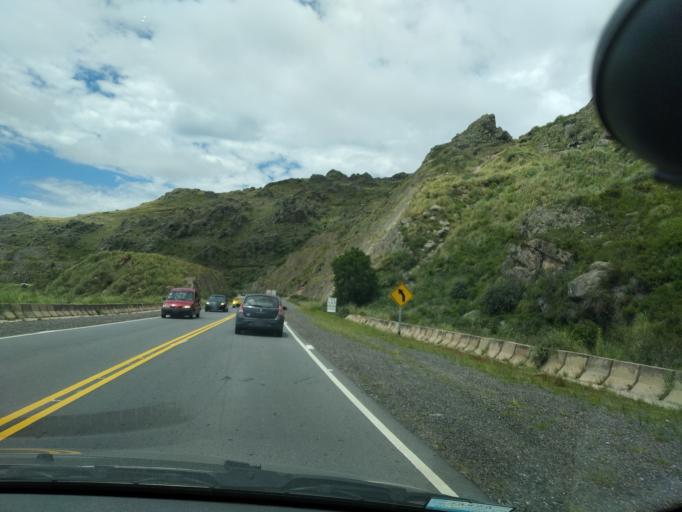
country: AR
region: Cordoba
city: Cuesta Blanca
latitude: -31.6117
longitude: -64.6926
